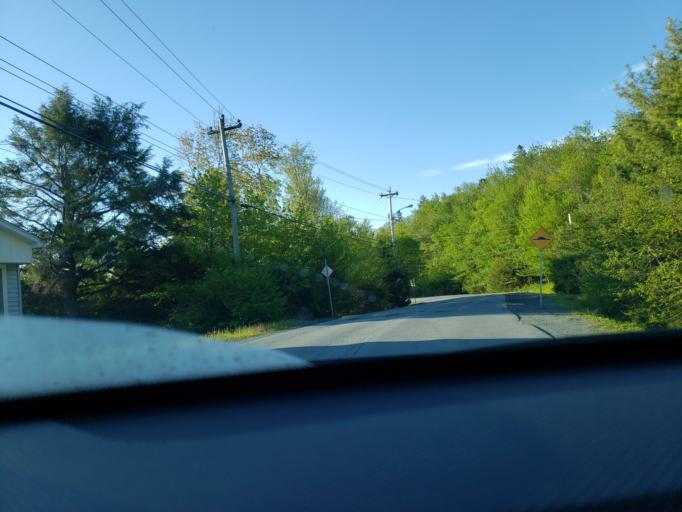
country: CA
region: Nova Scotia
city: Cole Harbour
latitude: 44.7444
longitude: -63.3804
